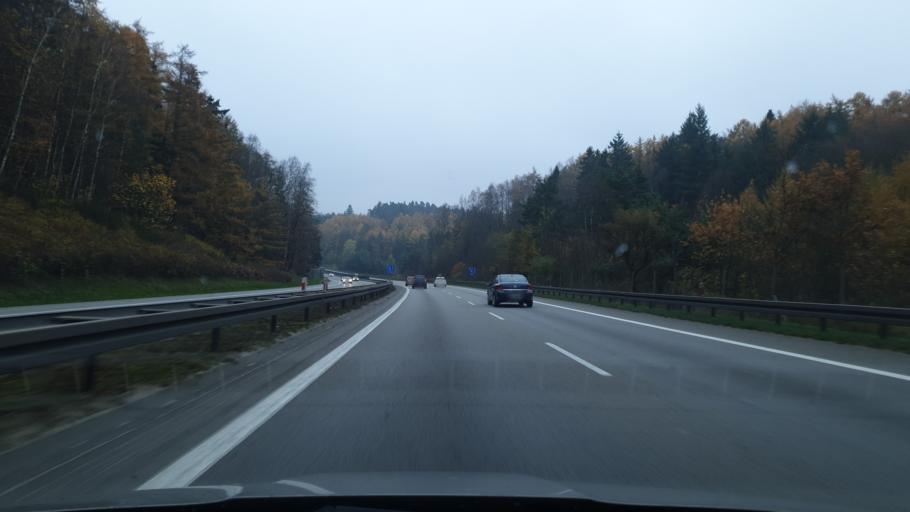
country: PL
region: Pomeranian Voivodeship
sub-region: Gdynia
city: Wielki Kack
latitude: 54.4941
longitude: 18.4620
